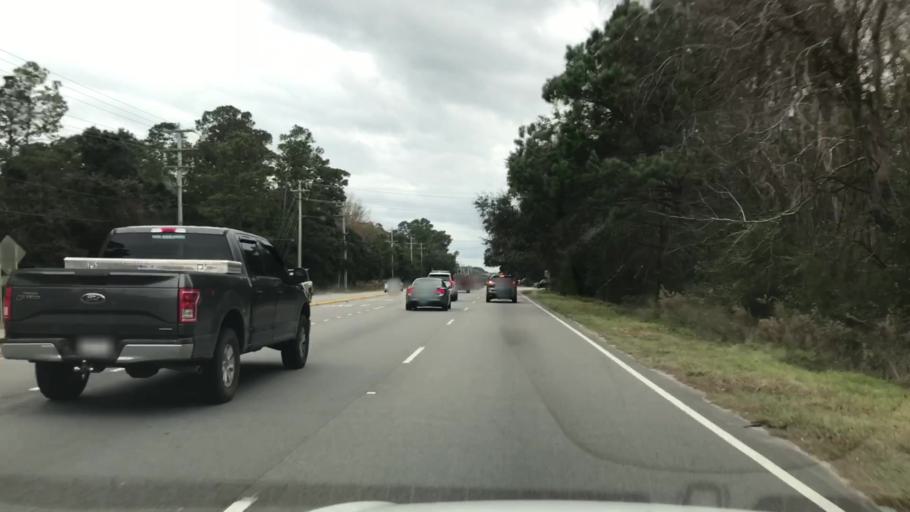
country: US
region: South Carolina
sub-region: Georgetown County
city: Murrells Inlet
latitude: 33.4554
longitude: -79.1157
